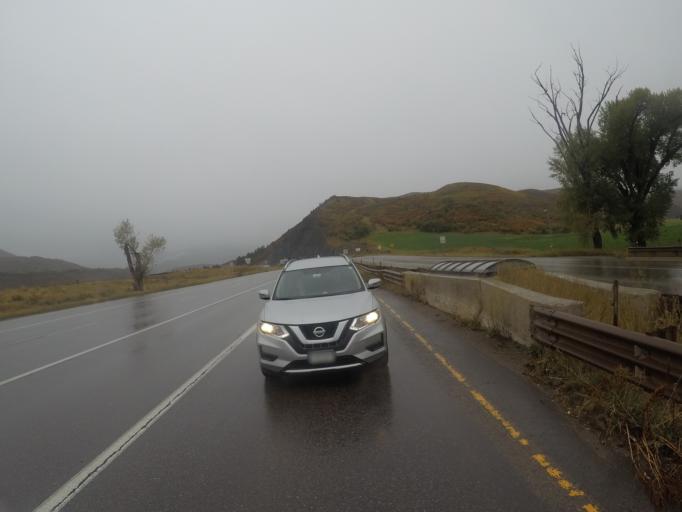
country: US
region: Colorado
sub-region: Pitkin County
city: Snowmass Village
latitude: 39.2491
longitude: -106.8838
